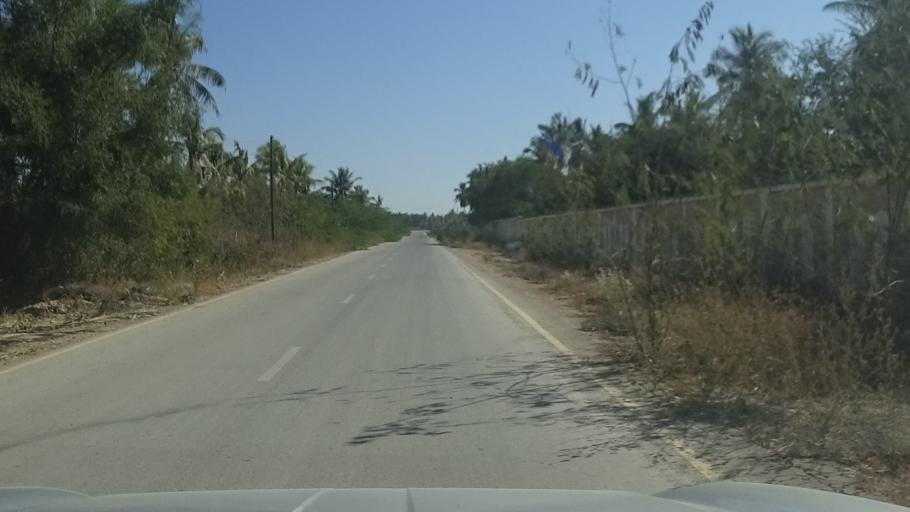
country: OM
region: Zufar
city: Salalah
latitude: 17.0327
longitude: 54.1476
